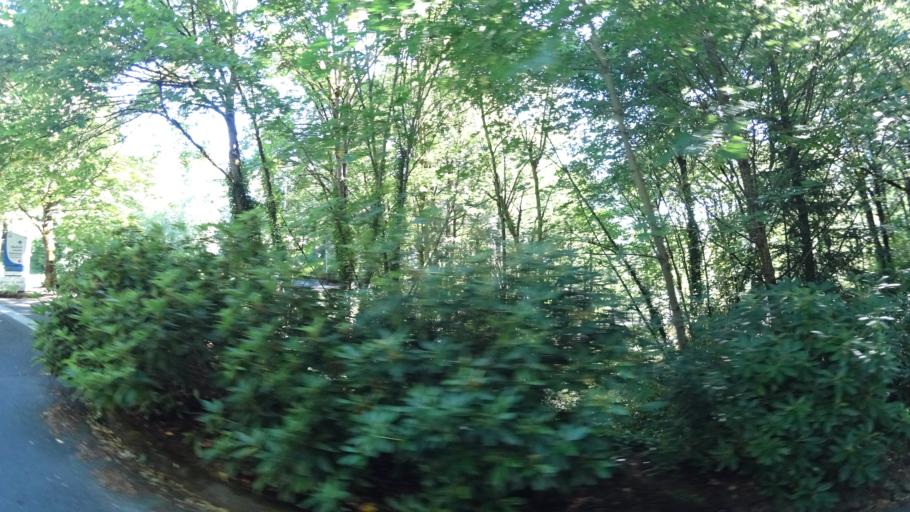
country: US
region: Oregon
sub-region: Multnomah County
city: Portland
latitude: 45.4945
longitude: -122.6834
